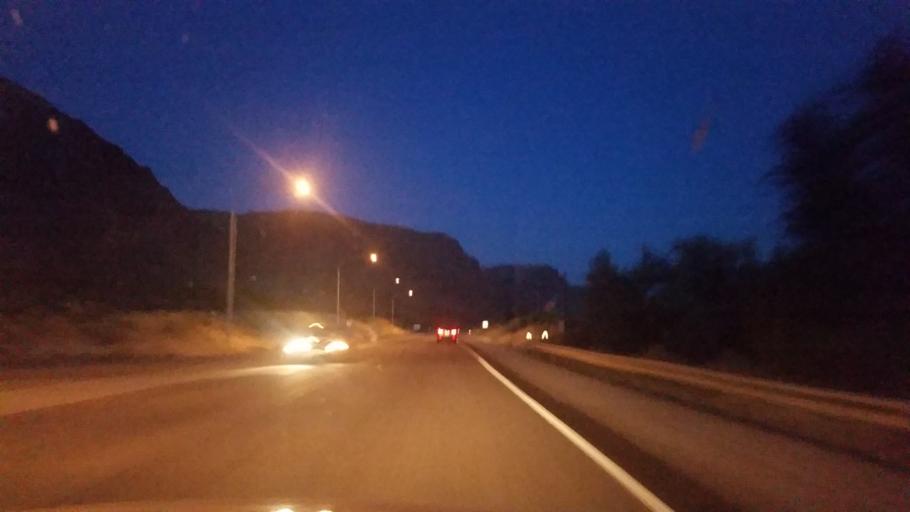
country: US
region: Washington
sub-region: Chelan County
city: South Wenatchee
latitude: 47.3650
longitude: -120.1212
